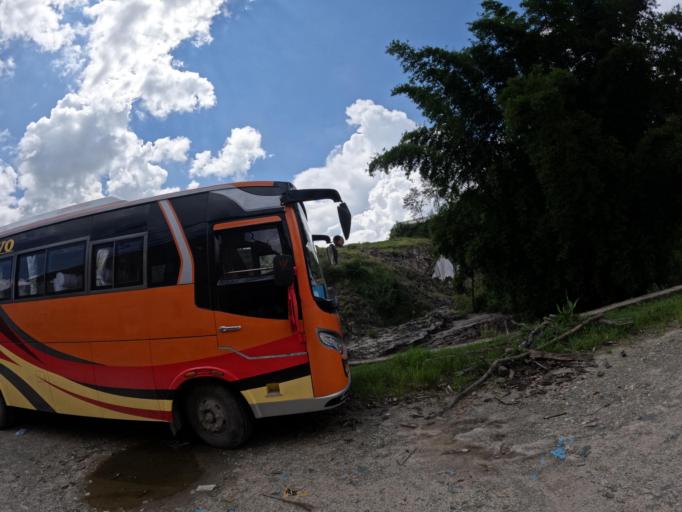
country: NP
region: Central Region
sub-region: Bagmati Zone
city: Kathmandu
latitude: 27.7818
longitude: 85.3272
